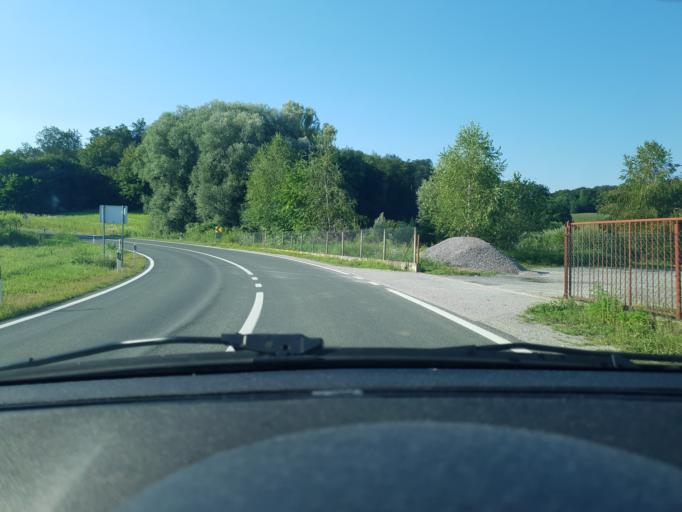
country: HR
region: Krapinsko-Zagorska
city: Radoboj
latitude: 46.1362
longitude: 15.9379
